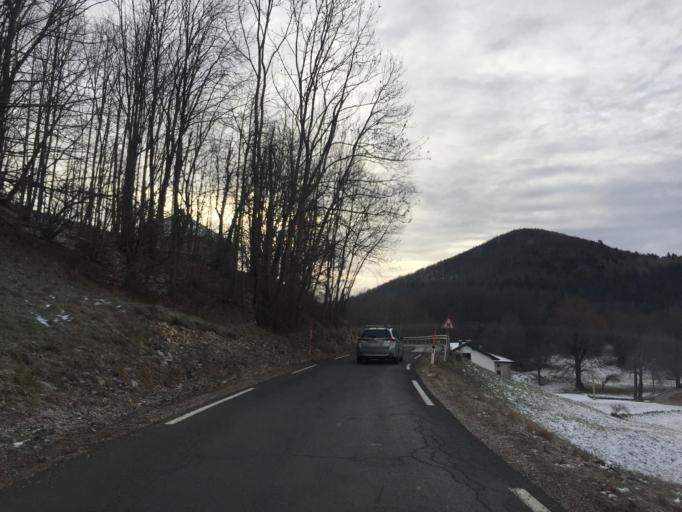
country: SI
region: Nova Gorica
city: Sempas
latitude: 46.0124
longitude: 13.7905
